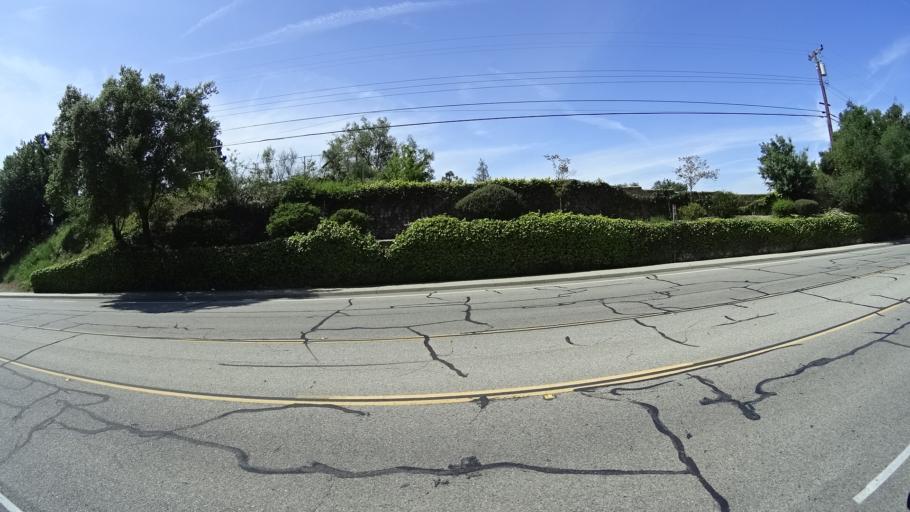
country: US
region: California
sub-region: Ventura County
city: Thousand Oaks
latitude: 34.1950
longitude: -118.8462
